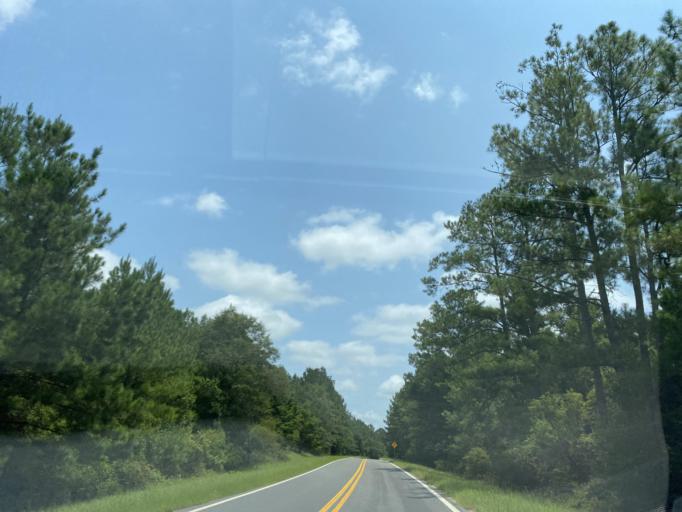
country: US
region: Georgia
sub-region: Telfair County
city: Lumber City
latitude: 31.9645
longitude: -82.7034
